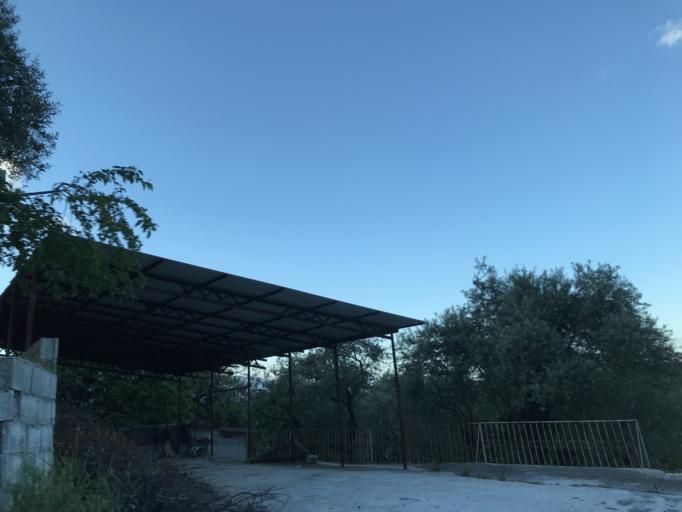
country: TR
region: Hatay
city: Buyukcat
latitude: 36.0995
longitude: 36.0642
